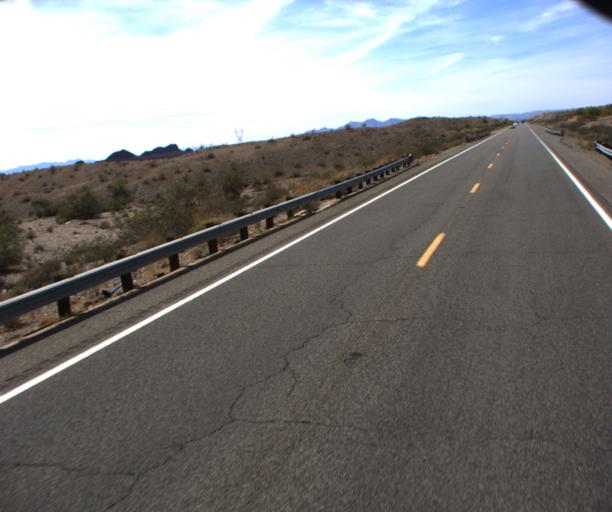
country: US
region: Arizona
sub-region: Mohave County
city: Lake Havasu City
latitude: 34.4373
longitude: -114.2243
